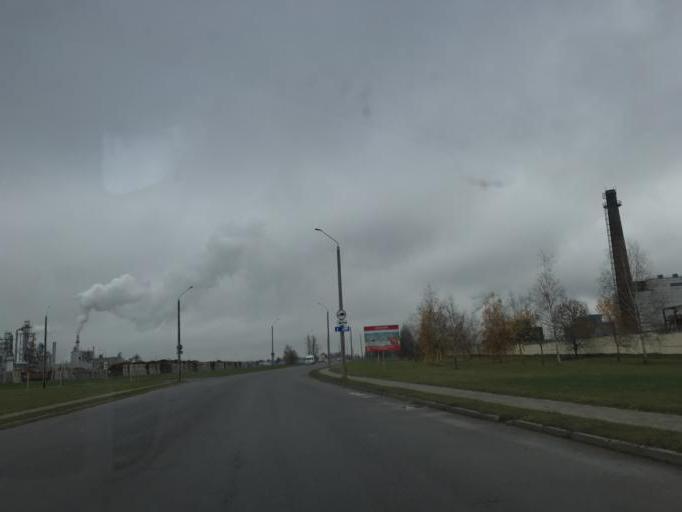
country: BY
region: Mogilev
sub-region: Mahilyowski Rayon
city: Veyno
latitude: 53.8286
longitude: 30.3386
